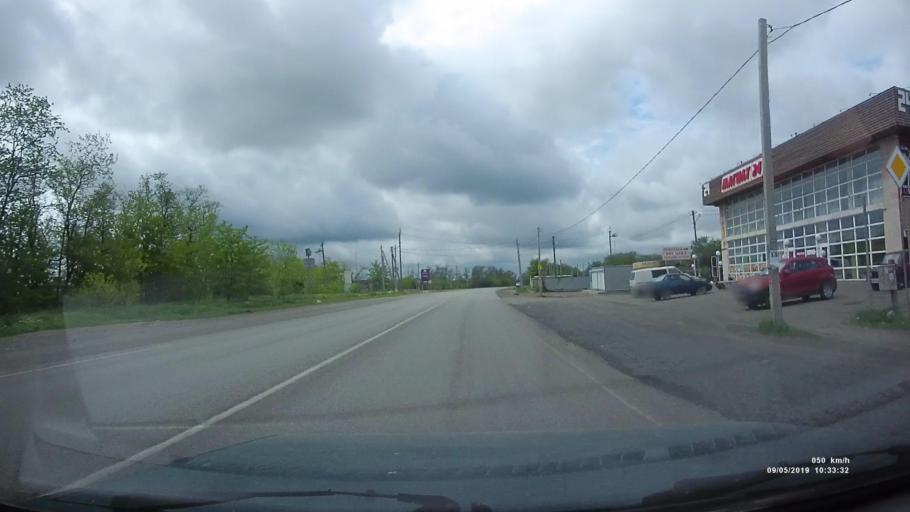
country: RU
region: Rostov
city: Azov
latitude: 47.0628
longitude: 39.4247
